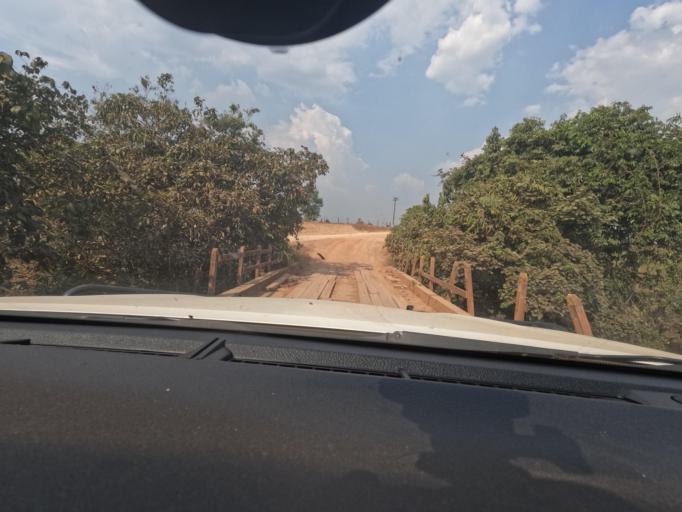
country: BR
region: Rondonia
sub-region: Porto Velho
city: Porto Velho
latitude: -8.6829
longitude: -63.1812
